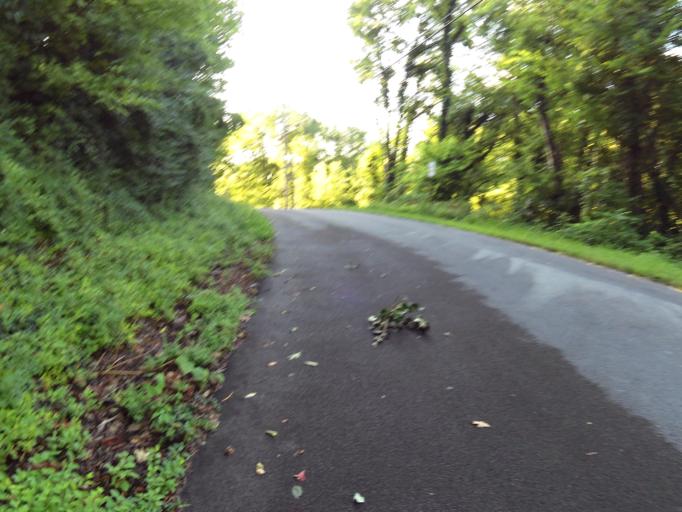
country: US
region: Tennessee
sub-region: Blount County
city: Eagleton Village
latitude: 35.8021
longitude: -83.9459
